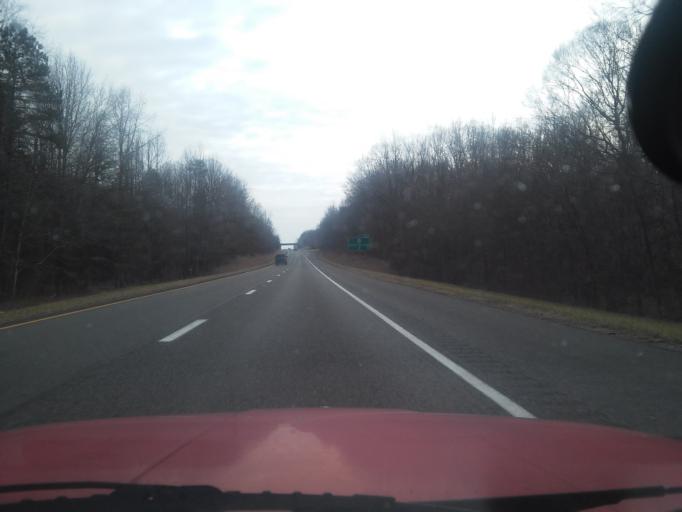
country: US
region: Virginia
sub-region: Louisa County
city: Louisa
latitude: 37.8900
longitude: -78.0382
